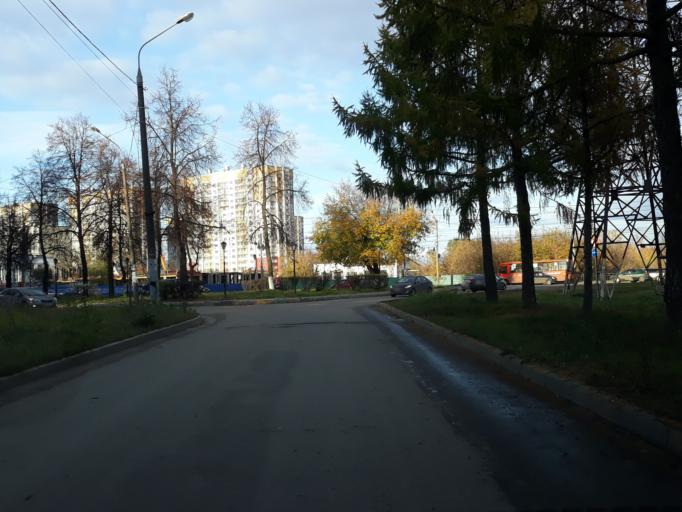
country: RU
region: Nizjnij Novgorod
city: Neklyudovo
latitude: 56.3439
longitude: 43.8727
